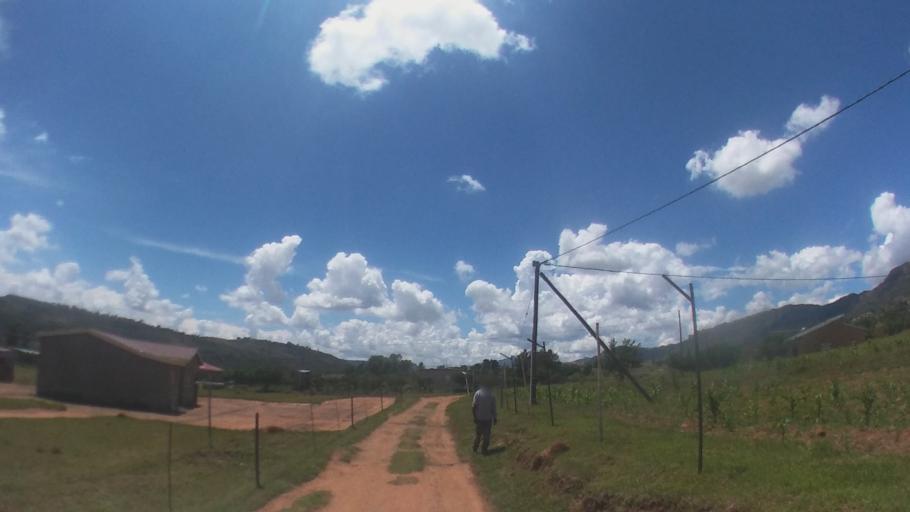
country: LS
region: Maseru
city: Nako
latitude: -29.6208
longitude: 27.5183
